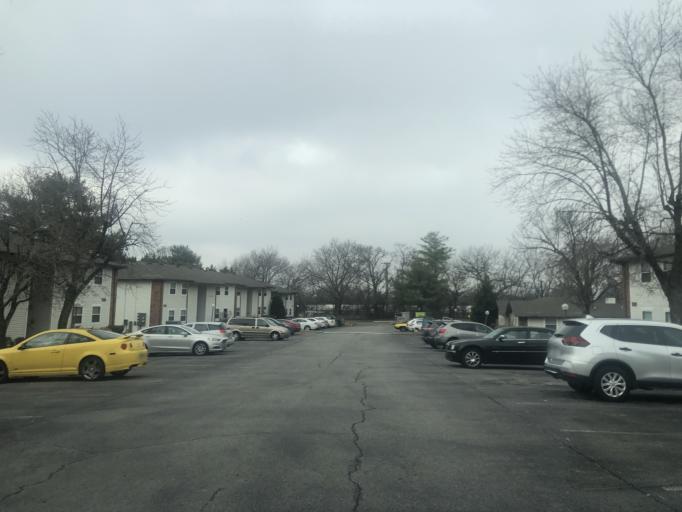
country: US
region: Tennessee
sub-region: Rutherford County
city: La Vergne
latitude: 36.0746
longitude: -86.6406
